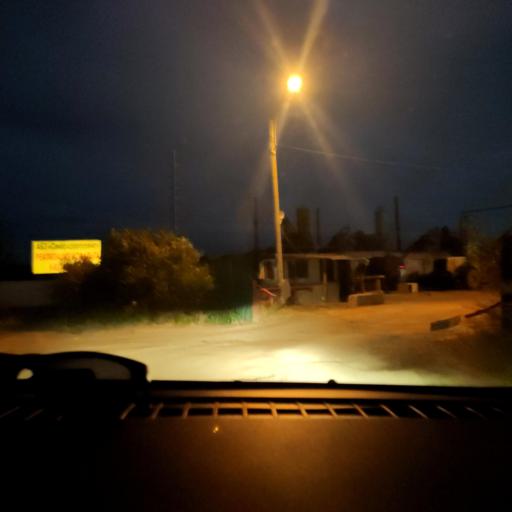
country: RU
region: Samara
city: Samara
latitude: 53.0667
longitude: 50.1409
